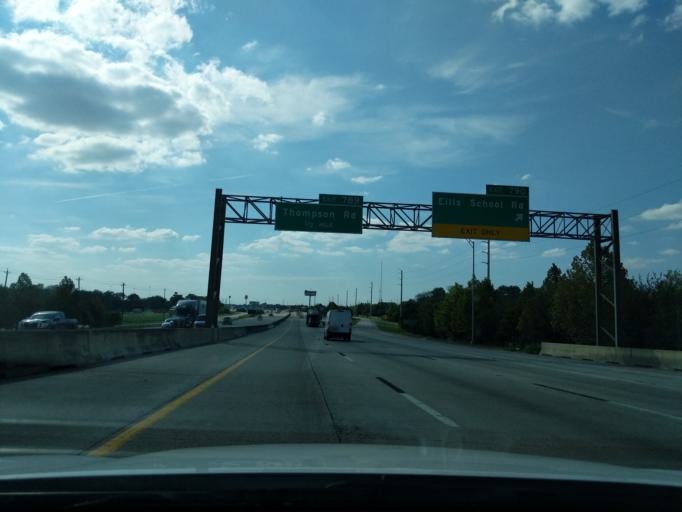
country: US
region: Texas
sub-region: Harris County
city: Highlands
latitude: 29.8000
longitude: -95.0199
